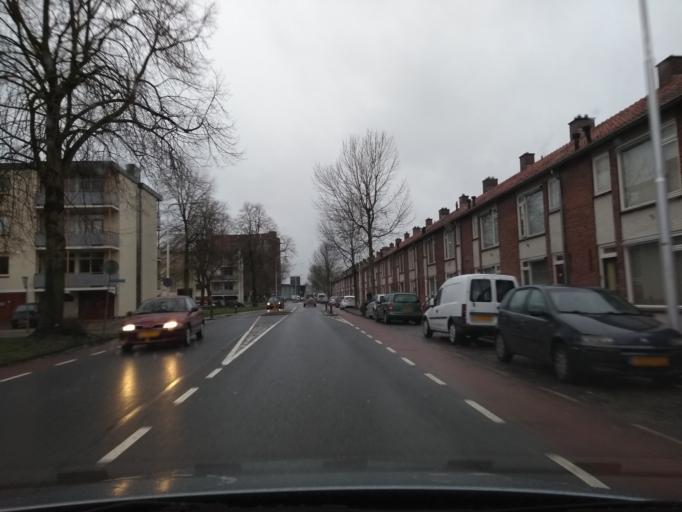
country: NL
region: Overijssel
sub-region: Gemeente Almelo
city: Almelo
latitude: 52.3488
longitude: 6.6445
